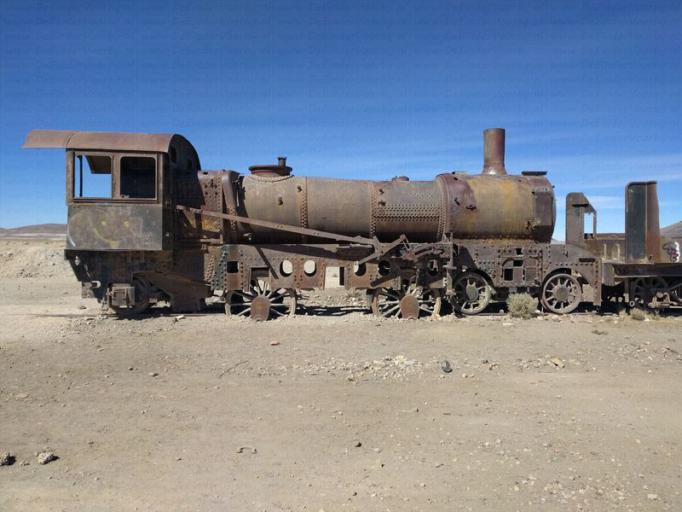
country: BO
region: Potosi
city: Uyuni
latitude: -20.4809
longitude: -66.8371
